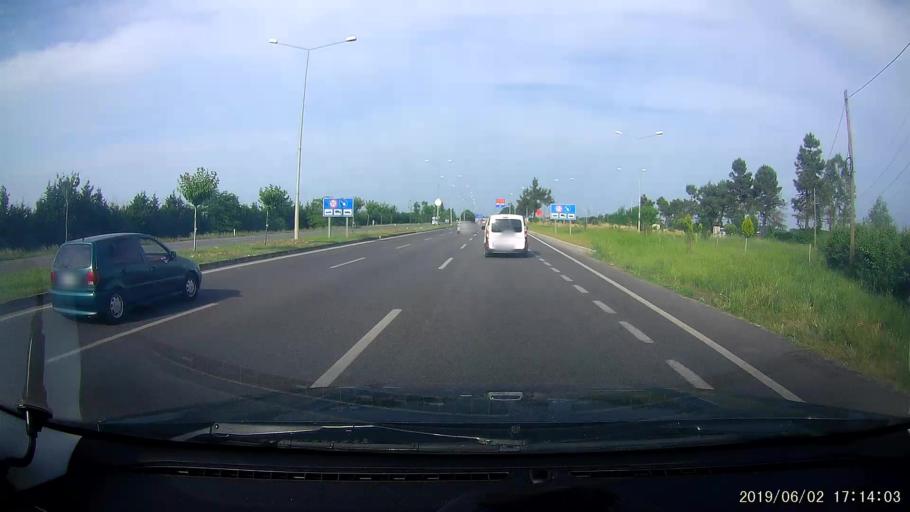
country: TR
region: Samsun
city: Tekkekoy
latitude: 41.2335
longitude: 36.5217
